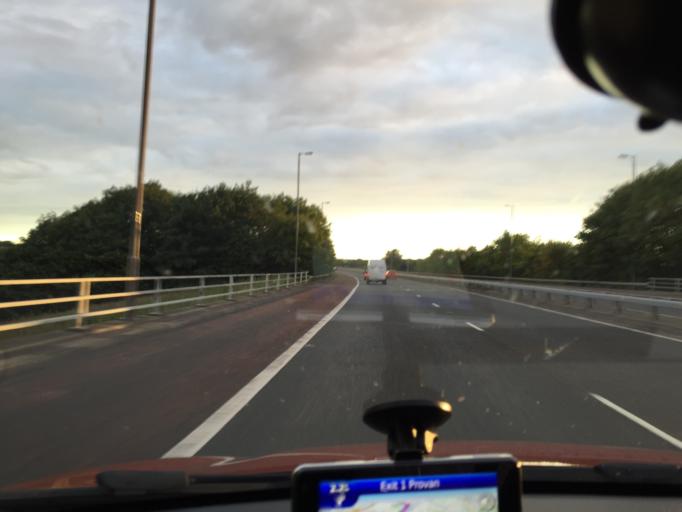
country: GB
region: Scotland
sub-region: North Lanarkshire
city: Stepps
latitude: 55.8903
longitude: -4.1783
